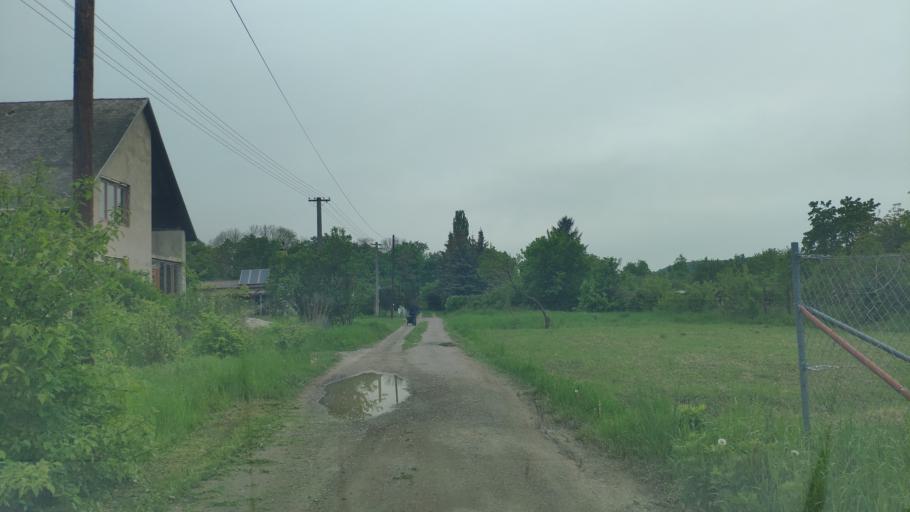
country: SK
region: Kosicky
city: Kosice
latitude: 48.6340
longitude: 21.1653
